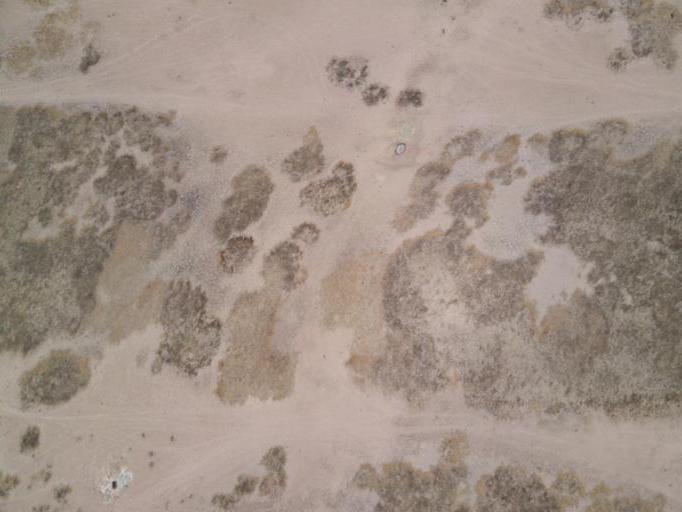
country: BO
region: La Paz
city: Batallas
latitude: -16.3569
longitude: -68.6281
